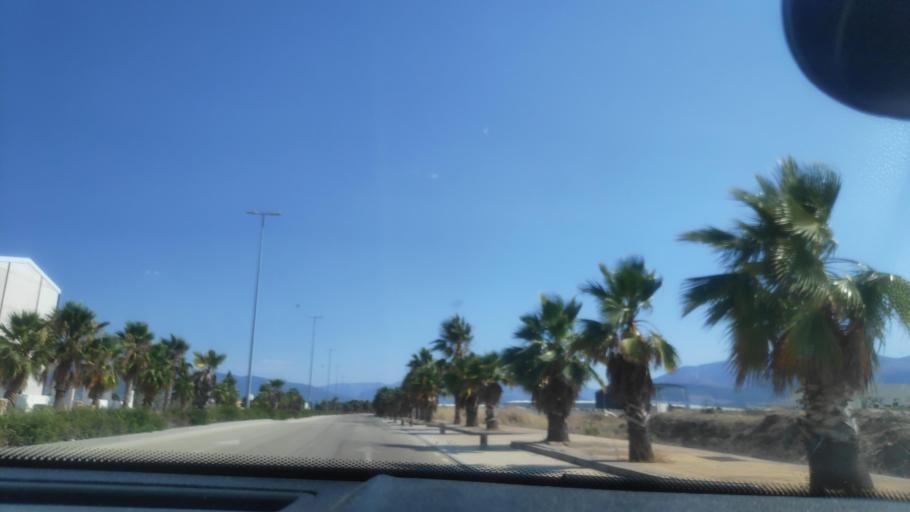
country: ES
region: Andalusia
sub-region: Provincia de Jaen
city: Jaen
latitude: 37.8252
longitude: -3.7762
